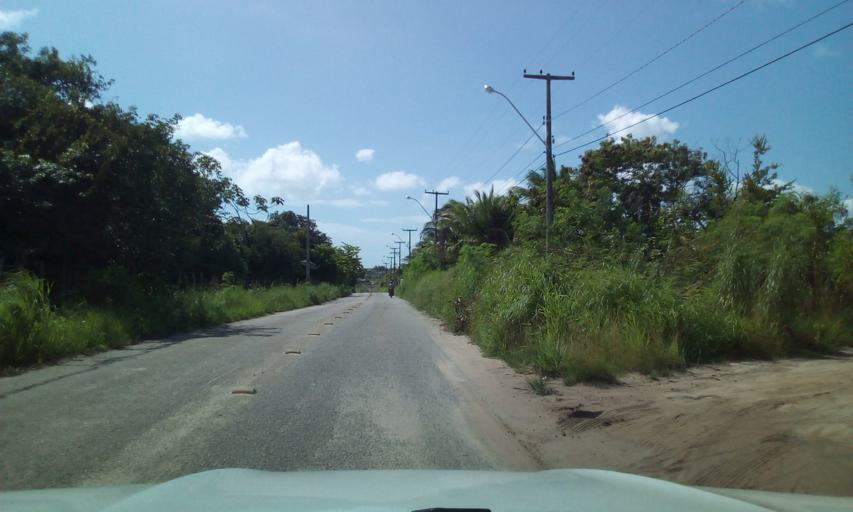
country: BR
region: Paraiba
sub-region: Conde
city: Conde
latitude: -7.2232
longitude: -34.8143
